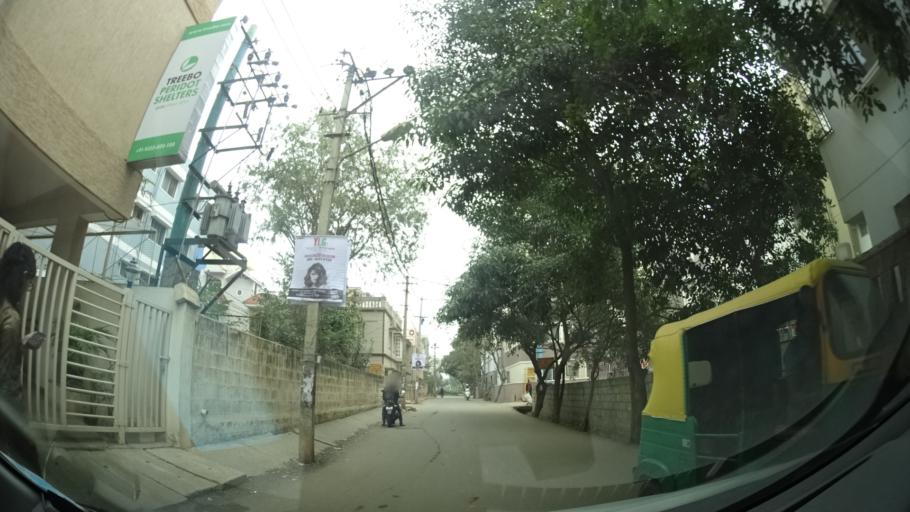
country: IN
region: Karnataka
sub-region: Bangalore Rural
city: Hoskote
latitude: 12.9826
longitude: 77.7486
